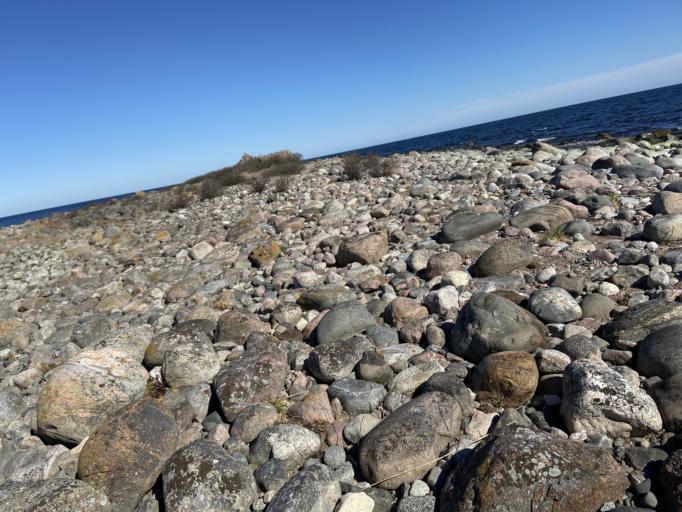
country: EE
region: Harju
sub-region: Loksa linn
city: Loksa
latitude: 59.6733
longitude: 25.6963
